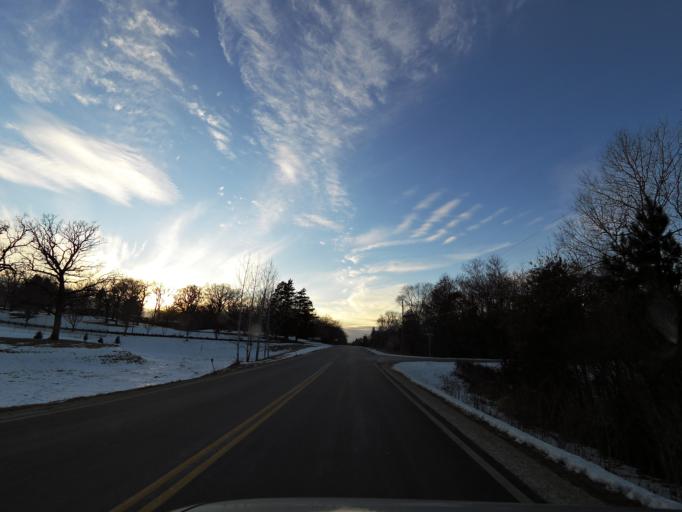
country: US
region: Minnesota
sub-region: Washington County
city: Lake Elmo
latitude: 44.9781
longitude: -92.8723
